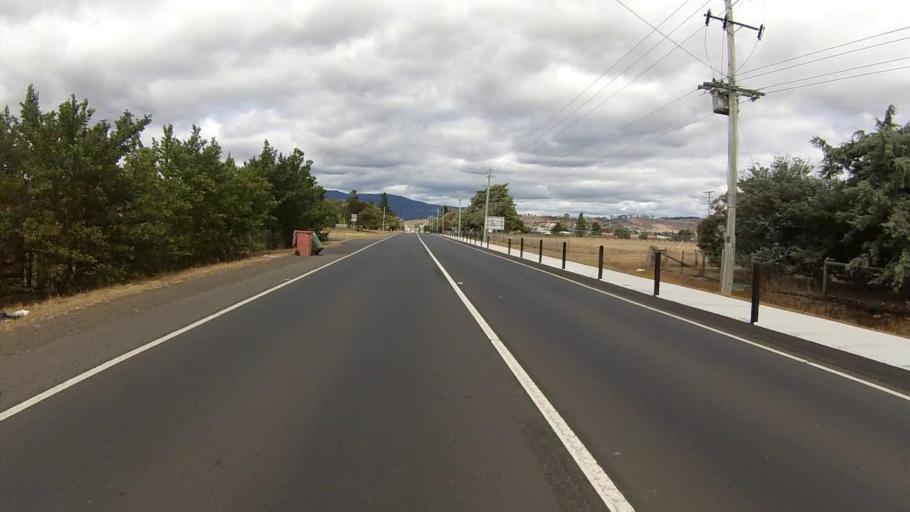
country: AU
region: Tasmania
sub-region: Brighton
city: Bridgewater
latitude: -42.6910
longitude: 147.2595
